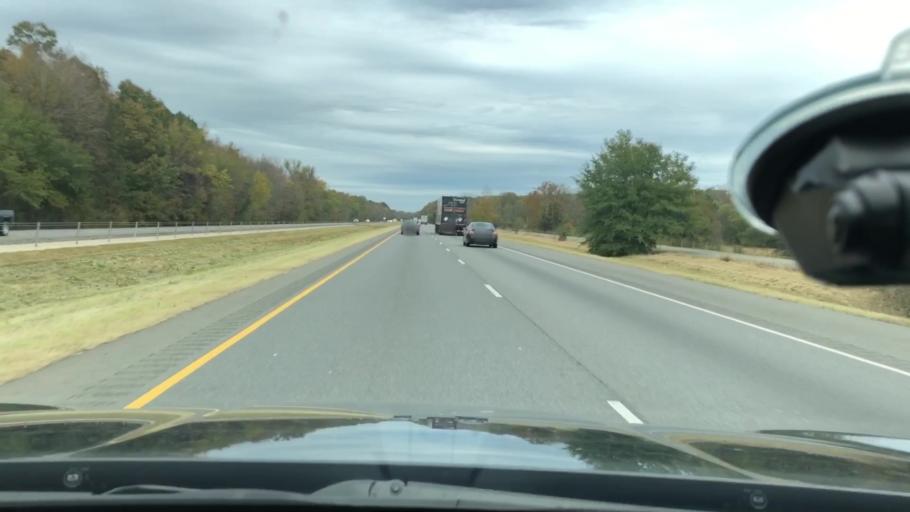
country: US
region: Arkansas
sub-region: Hot Spring County
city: Malvern
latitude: 34.3615
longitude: -92.8744
